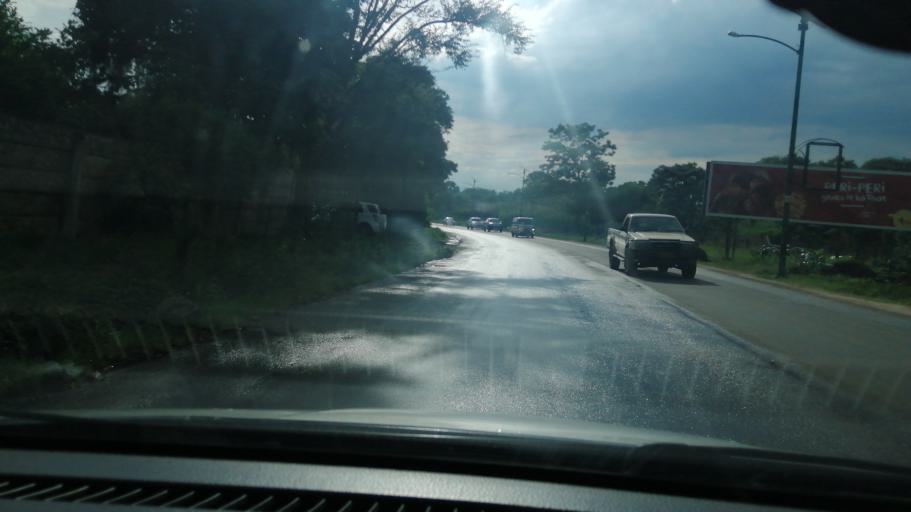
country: ZW
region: Harare
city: Harare
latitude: -17.7906
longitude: 31.0465
